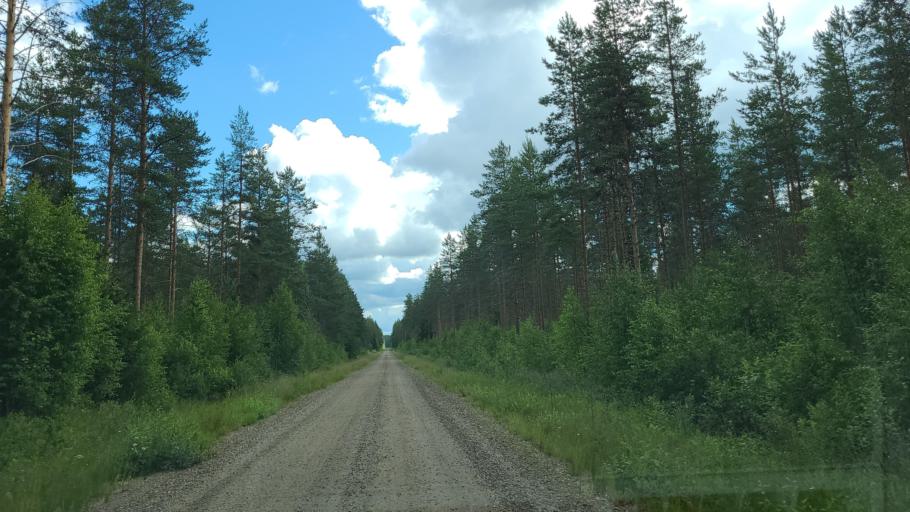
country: FI
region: Northern Savo
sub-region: Koillis-Savo
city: Kaavi
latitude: 63.0272
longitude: 28.7584
